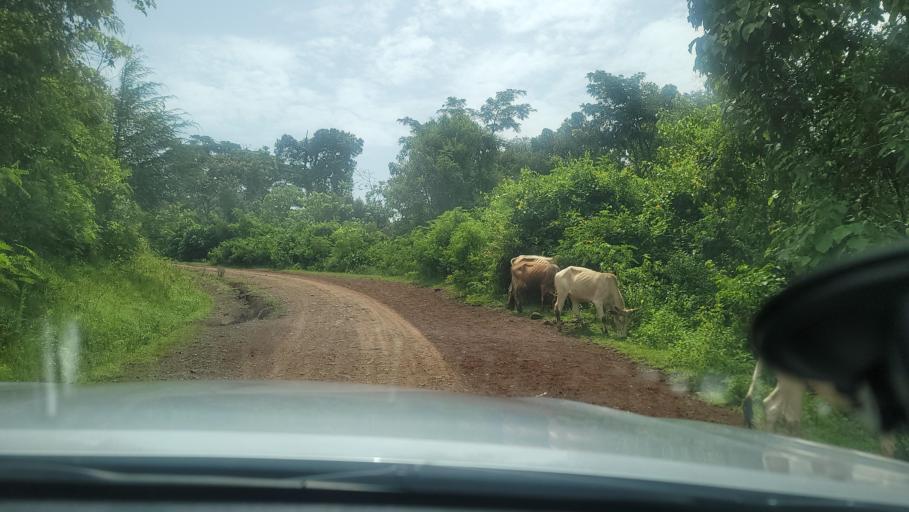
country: ET
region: Oromiya
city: Agaro
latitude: 7.8125
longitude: 36.4120
